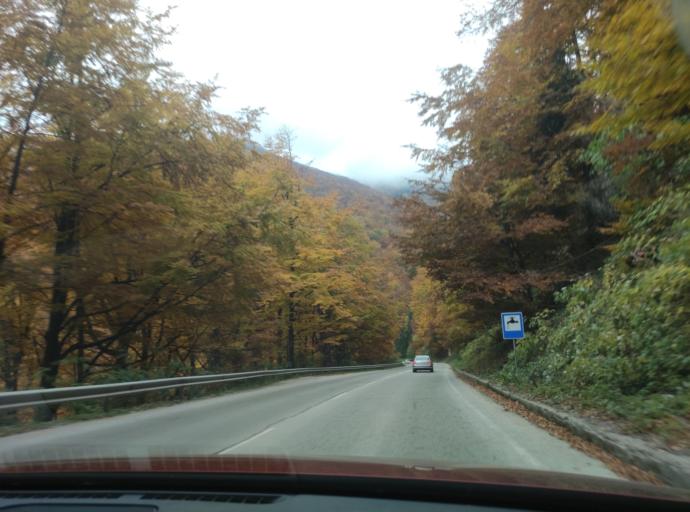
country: BG
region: Montana
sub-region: Obshtina Berkovitsa
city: Berkovitsa
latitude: 43.1285
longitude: 23.1373
